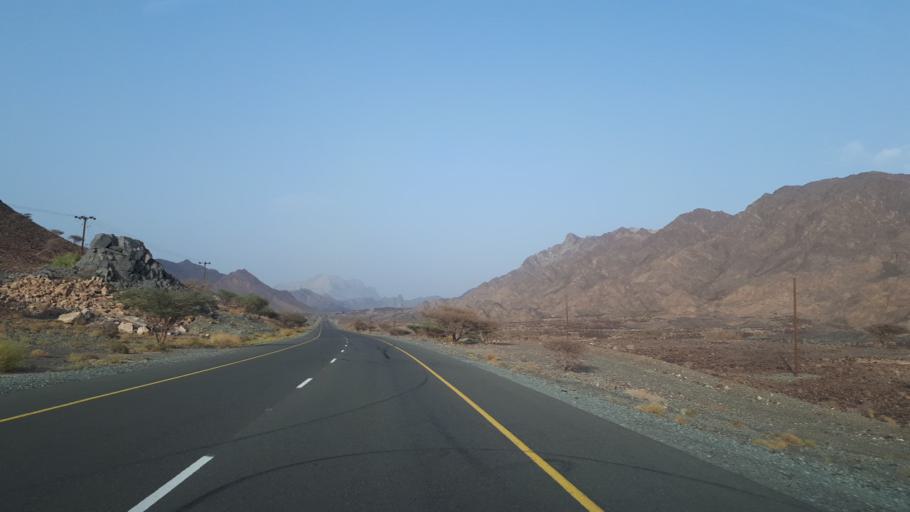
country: OM
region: Az Zahirah
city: Yanqul
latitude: 23.4919
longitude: 56.8725
